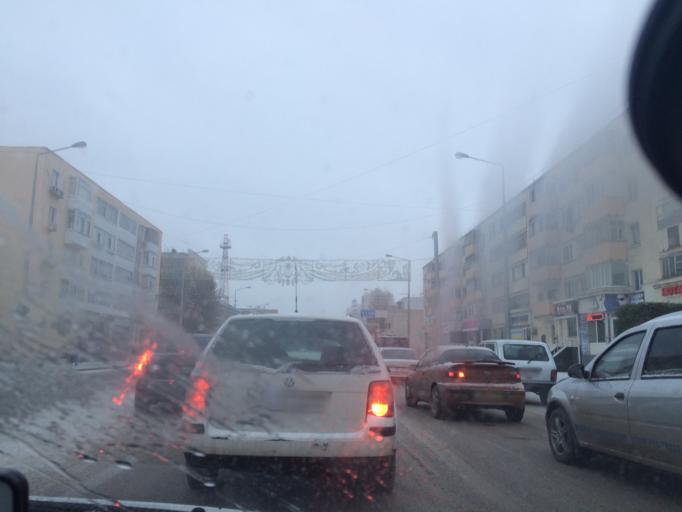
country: KZ
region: Astana Qalasy
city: Astana
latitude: 51.1735
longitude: 71.4068
